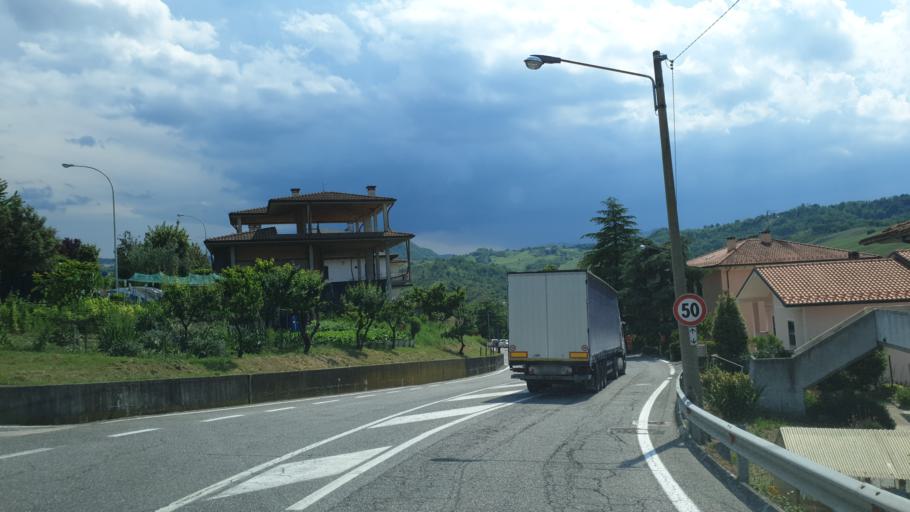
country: SM
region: Acquaviva
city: Acquaviva
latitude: 43.9493
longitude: 12.4093
